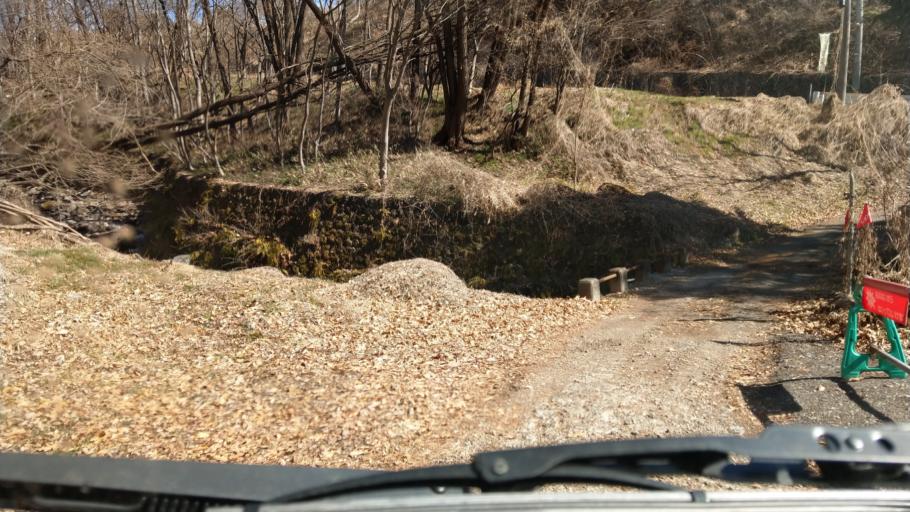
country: JP
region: Nagano
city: Komoro
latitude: 36.3356
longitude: 138.3918
